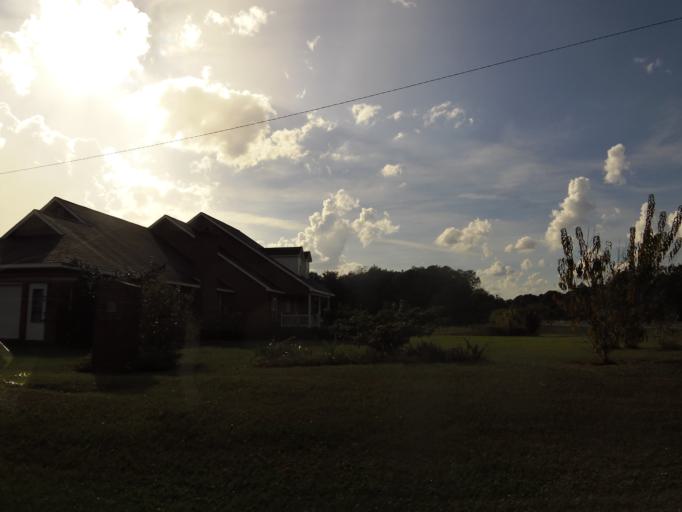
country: US
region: Georgia
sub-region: Brooks County
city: Quitman
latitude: 30.7880
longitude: -83.6354
